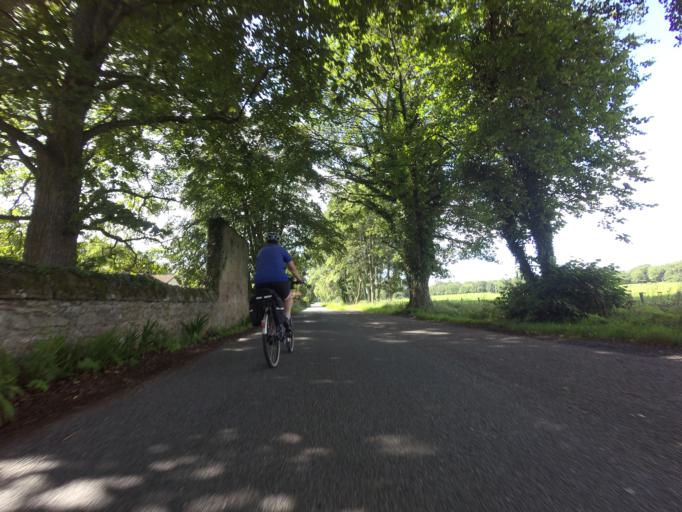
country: GB
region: Scotland
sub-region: Highland
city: Nairn
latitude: 57.5758
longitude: -3.8619
